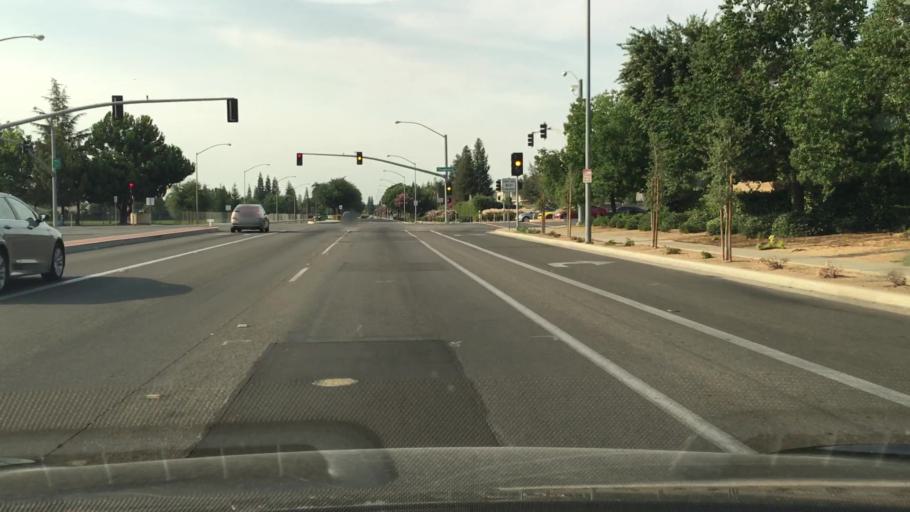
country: US
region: California
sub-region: Fresno County
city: Clovis
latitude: 36.8660
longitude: -119.7387
